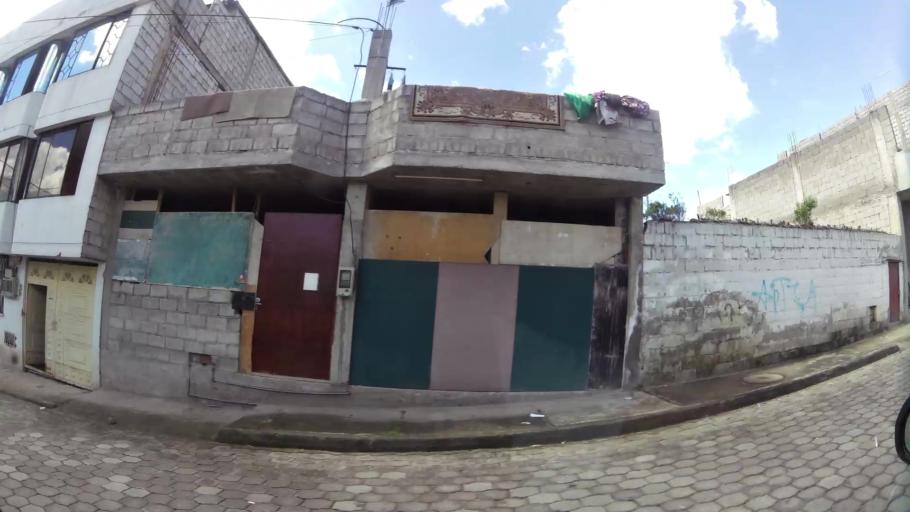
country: EC
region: Pichincha
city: Quito
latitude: -0.3252
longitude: -78.5611
